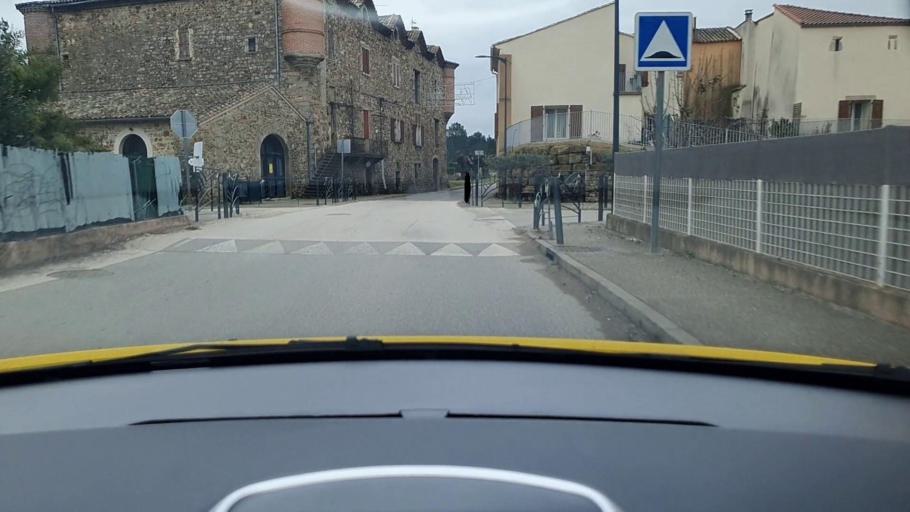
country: FR
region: Languedoc-Roussillon
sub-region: Departement du Gard
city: Laval-Pradel
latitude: 44.2304
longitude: 4.0598
